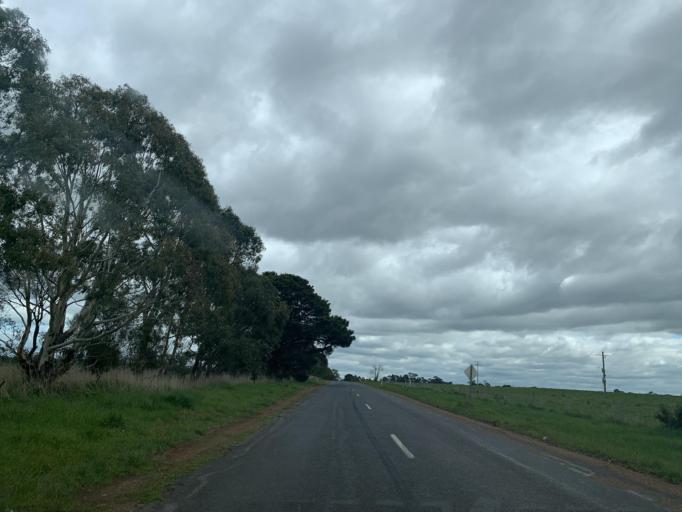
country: AU
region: Victoria
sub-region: Whittlesea
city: Whittlesea
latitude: -37.1859
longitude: 145.0367
